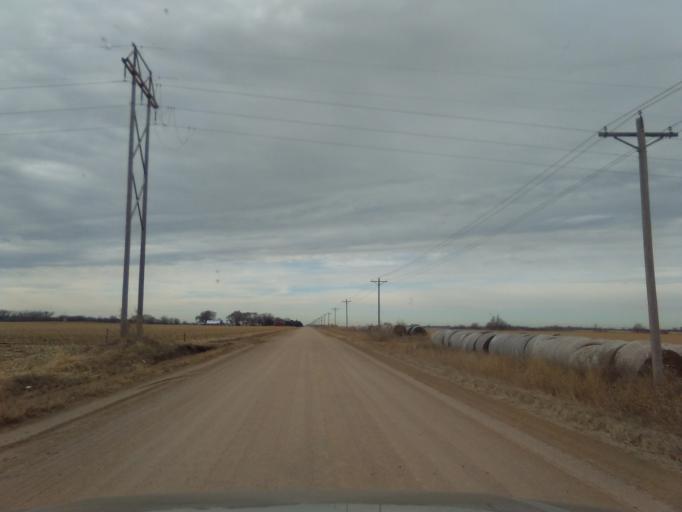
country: US
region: Nebraska
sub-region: Buffalo County
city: Gibbon
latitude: 40.6407
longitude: -98.8848
